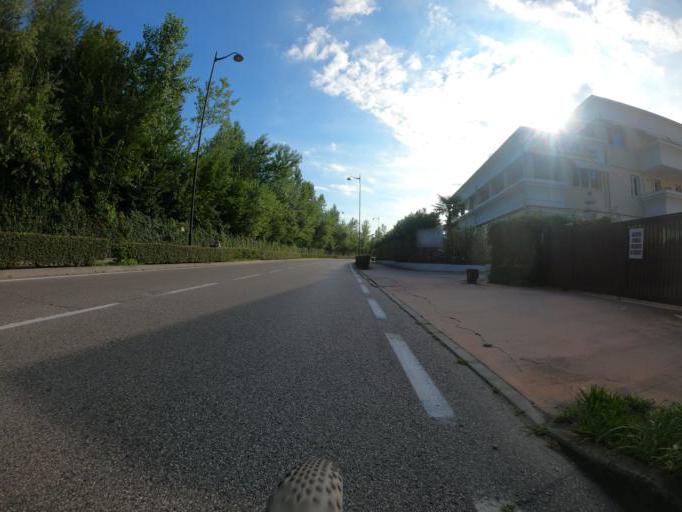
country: IT
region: Lombardy
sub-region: Provincia di Brescia
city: San Martino della Battaglia
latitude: 45.4628
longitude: 10.5882
